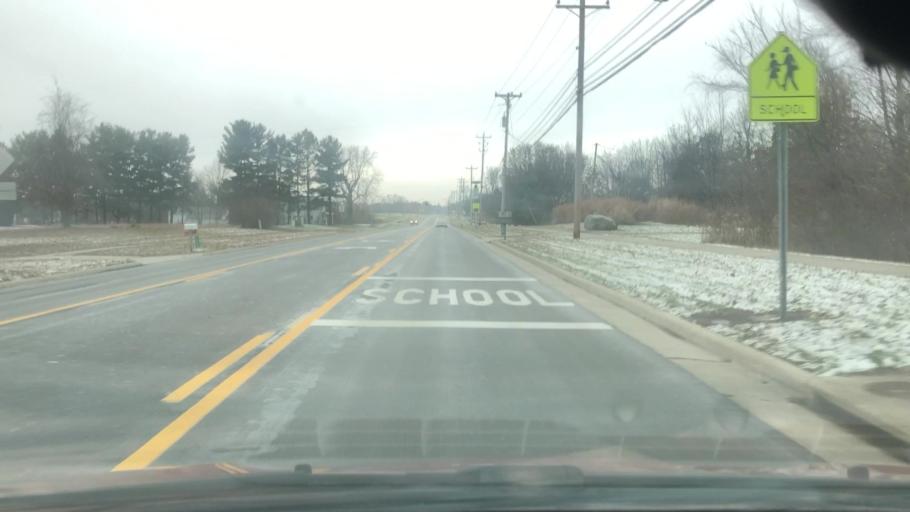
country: US
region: Ohio
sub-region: Franklin County
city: Westerville
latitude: 40.1525
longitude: -82.9009
